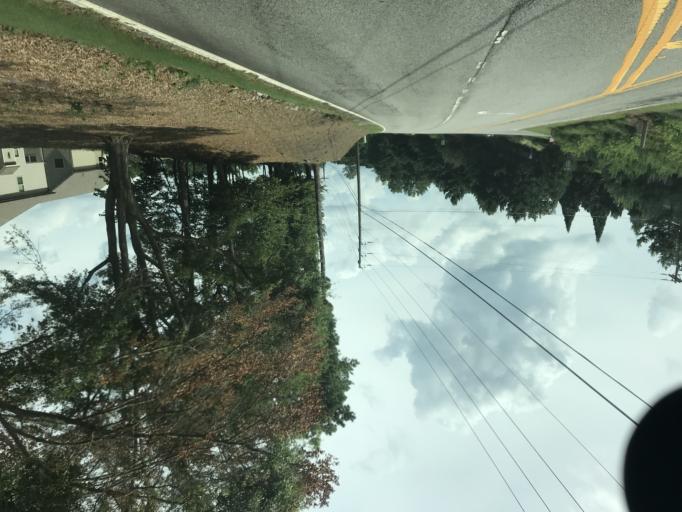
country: US
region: Georgia
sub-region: Forsyth County
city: Cumming
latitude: 34.2269
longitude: -84.2429
